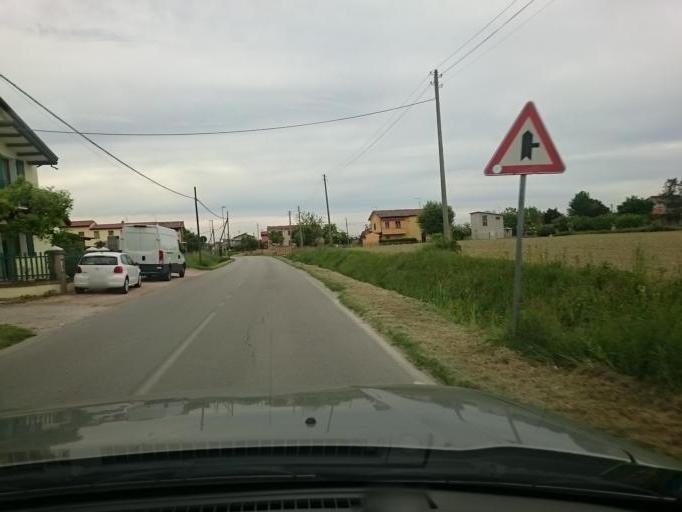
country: IT
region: Veneto
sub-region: Provincia di Padova
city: Bertipaglia
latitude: 45.3202
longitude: 11.8852
